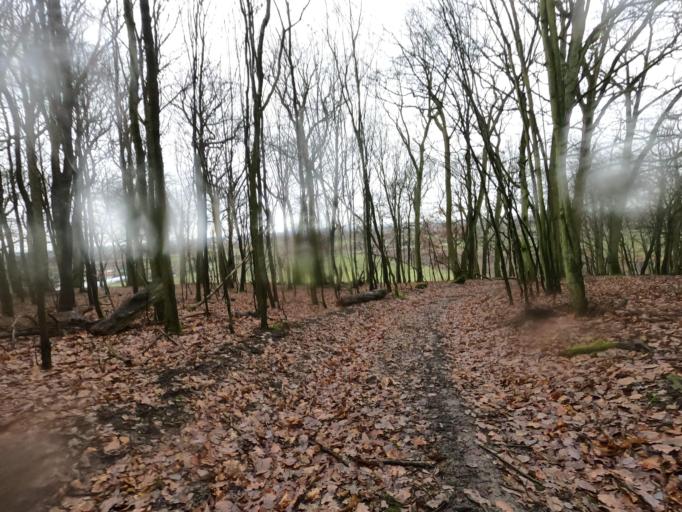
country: PL
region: Greater Poland Voivodeship
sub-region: Powiat pilski
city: Osiek nad Notecia
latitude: 53.1181
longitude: 17.2623
